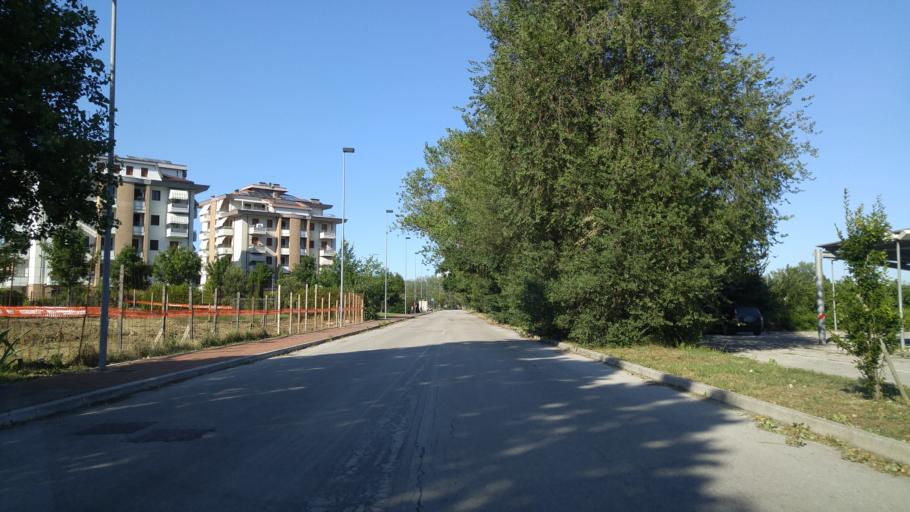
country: IT
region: The Marches
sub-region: Provincia di Pesaro e Urbino
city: Pesaro
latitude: 43.9015
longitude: 12.8629
